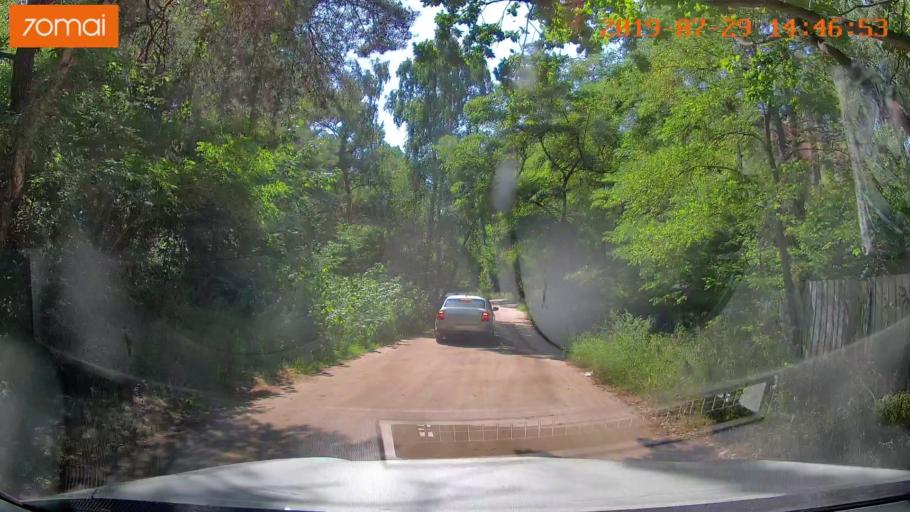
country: RU
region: Kaliningrad
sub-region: Gorod Kaliningrad
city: Baltiysk
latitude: 54.6635
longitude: 19.9017
